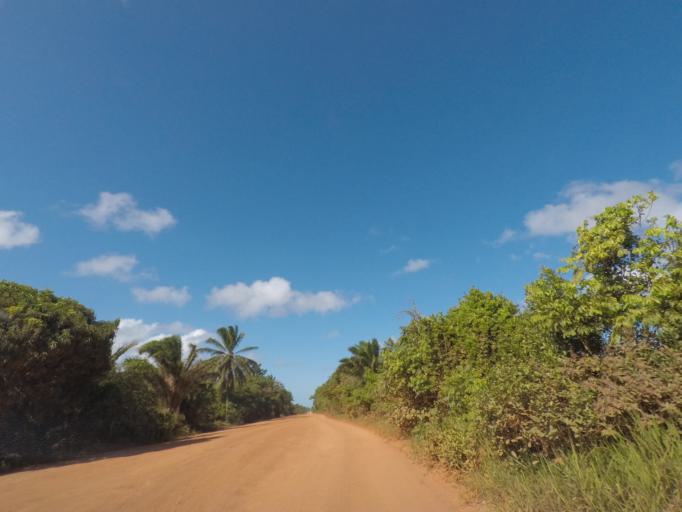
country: BR
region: Bahia
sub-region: Marau
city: Marau
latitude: -14.1561
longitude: -39.0093
